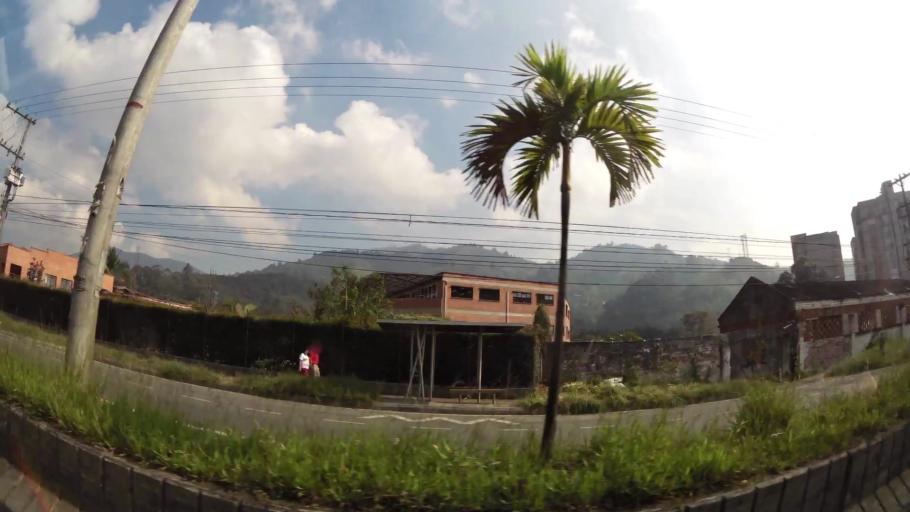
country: CO
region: Antioquia
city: La Estrella
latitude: 6.1726
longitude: -75.6305
